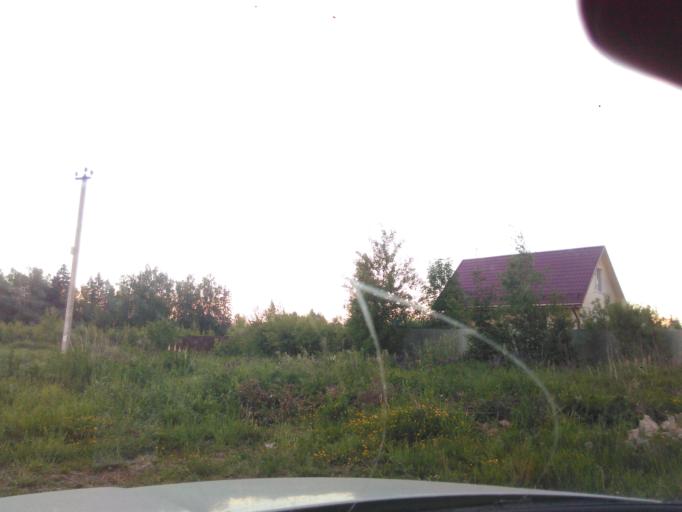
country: RU
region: Moskovskaya
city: Mendeleyevo
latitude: 56.0933
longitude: 37.2685
